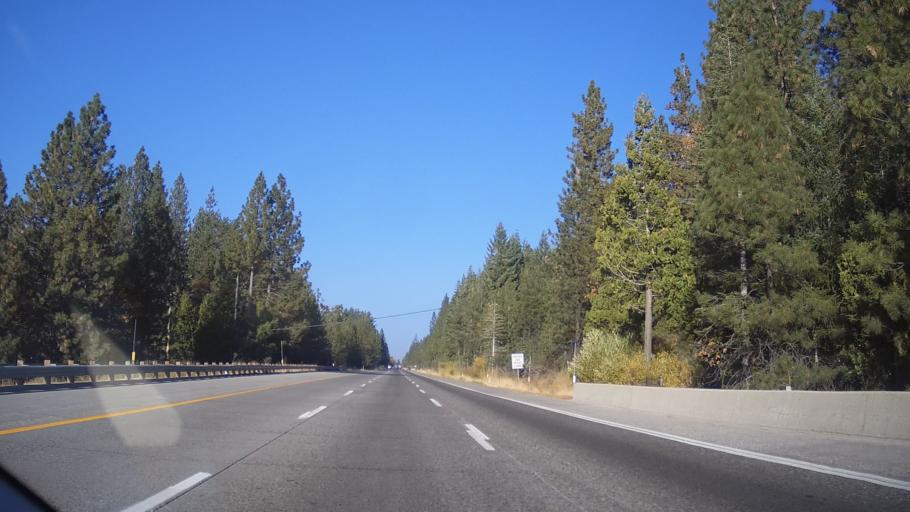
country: US
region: California
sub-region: Placer County
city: Foresthill
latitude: 39.2575
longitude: -120.7307
